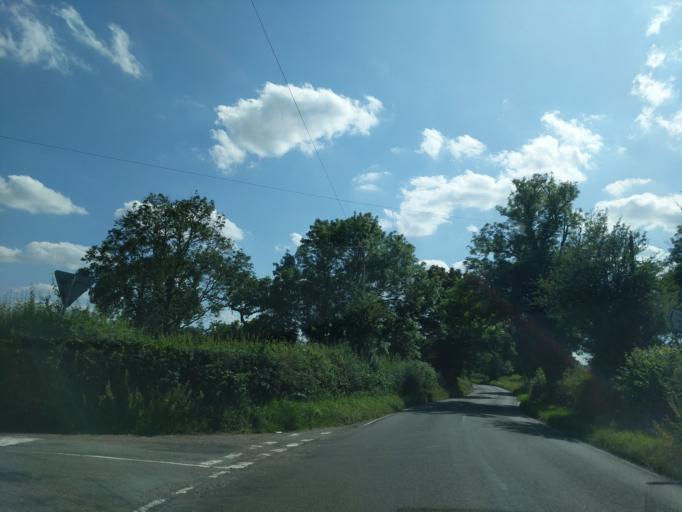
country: GB
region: England
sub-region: Staffordshire
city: Rugeley
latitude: 52.7907
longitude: -1.9350
